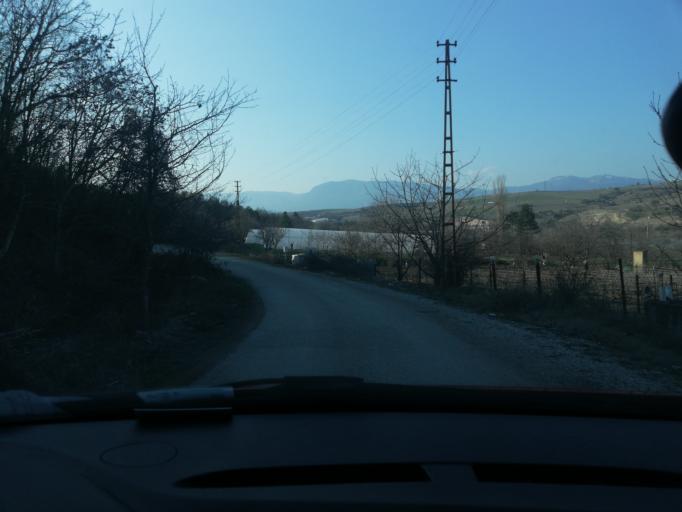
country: TR
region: Karabuk
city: Safranbolu
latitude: 41.2135
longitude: 32.7481
